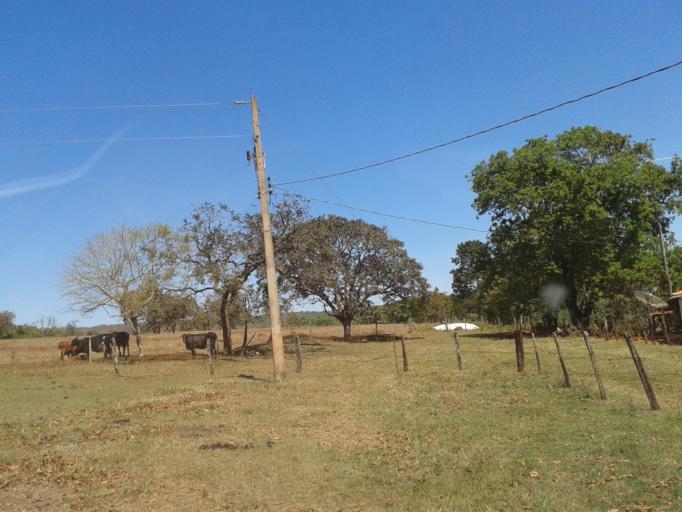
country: BR
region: Minas Gerais
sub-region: Ituiutaba
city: Ituiutaba
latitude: -19.1134
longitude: -49.2803
